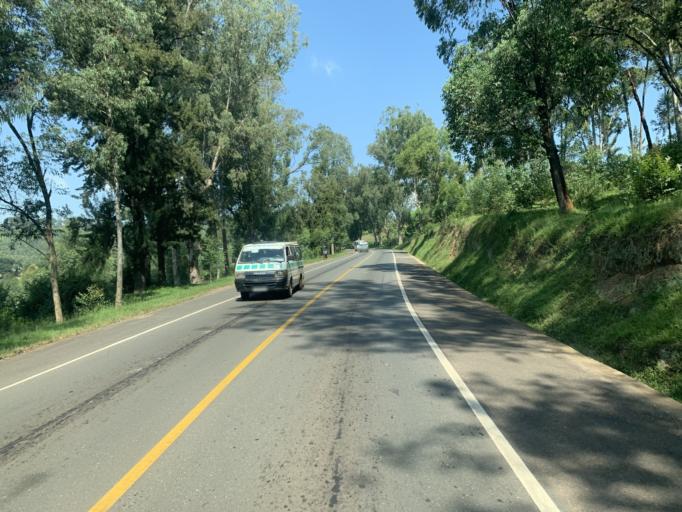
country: RW
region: Kigali
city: Kigali
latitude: -1.9941
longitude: 29.9249
